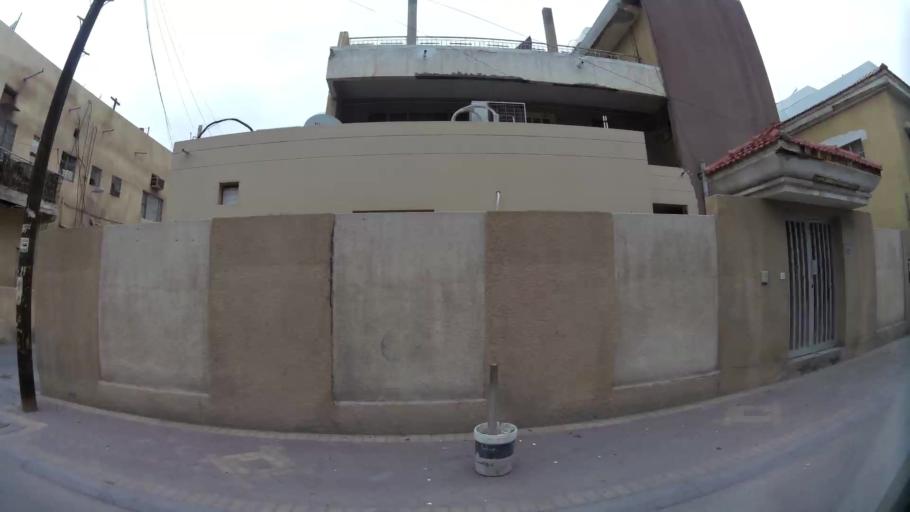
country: BH
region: Manama
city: Jidd Hafs
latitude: 26.2203
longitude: 50.5654
